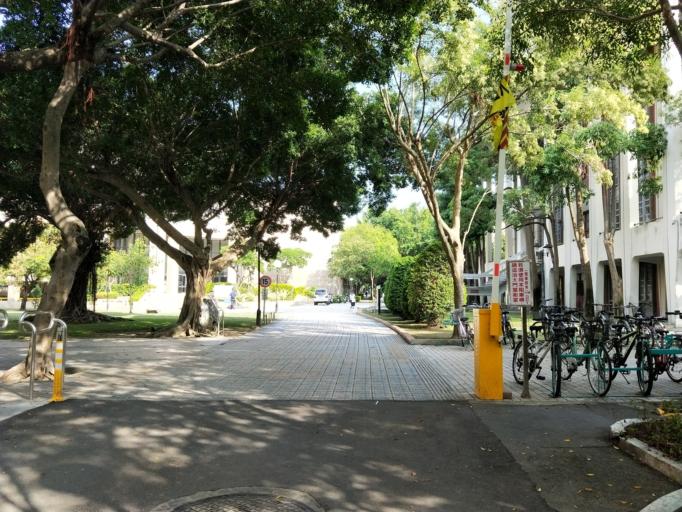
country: TW
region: Taiwan
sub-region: Changhua
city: Chang-hua
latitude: 24.0803
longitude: 120.5579
